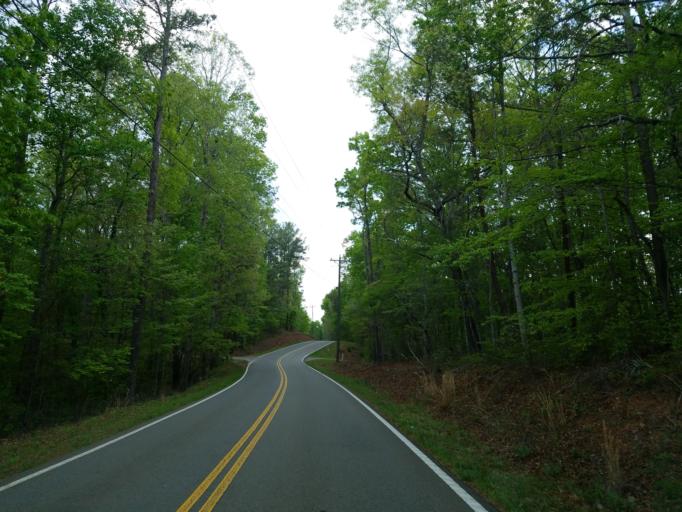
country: US
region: Georgia
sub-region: Pickens County
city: Jasper
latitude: 34.4320
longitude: -84.4584
